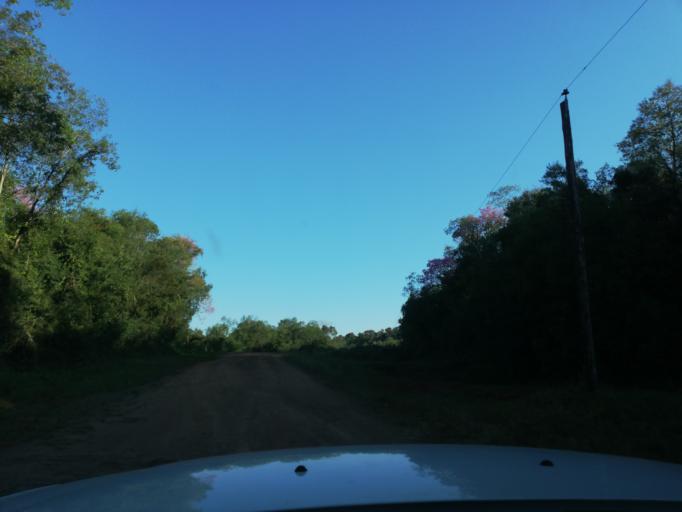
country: AR
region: Misiones
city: Cerro Cora
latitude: -27.6124
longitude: -55.7058
